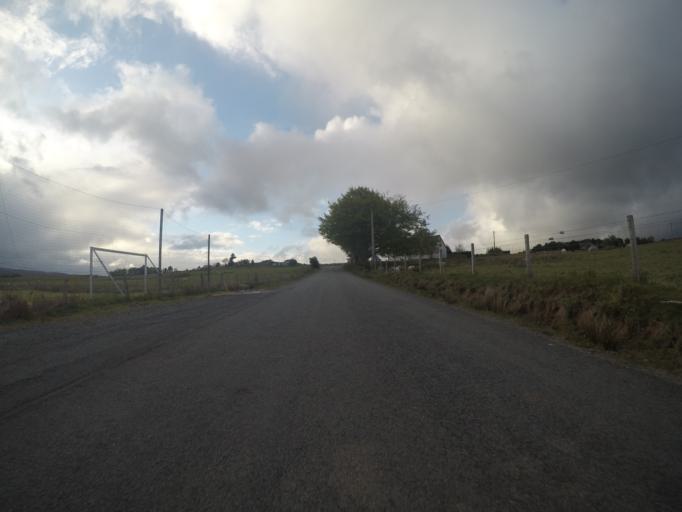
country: GB
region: Scotland
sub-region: Highland
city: Isle of Skye
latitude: 57.4544
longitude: -6.2977
